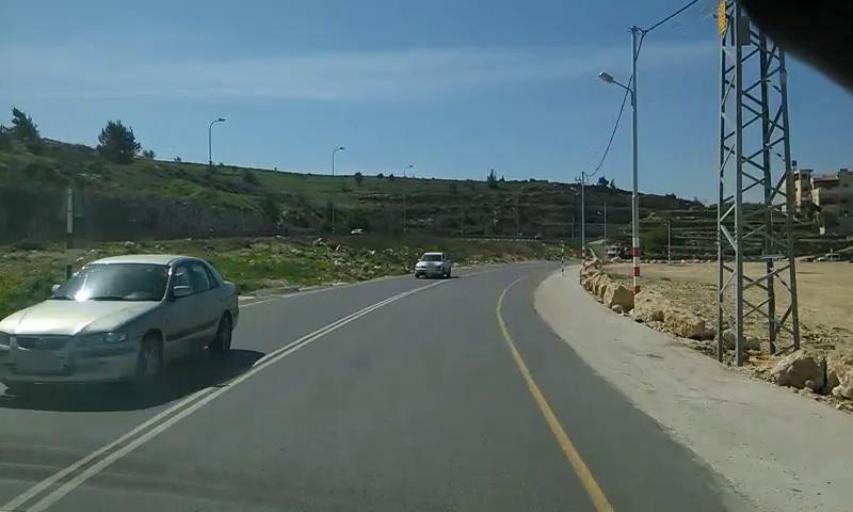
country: PS
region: West Bank
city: Battir
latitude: 31.7067
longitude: 35.1519
